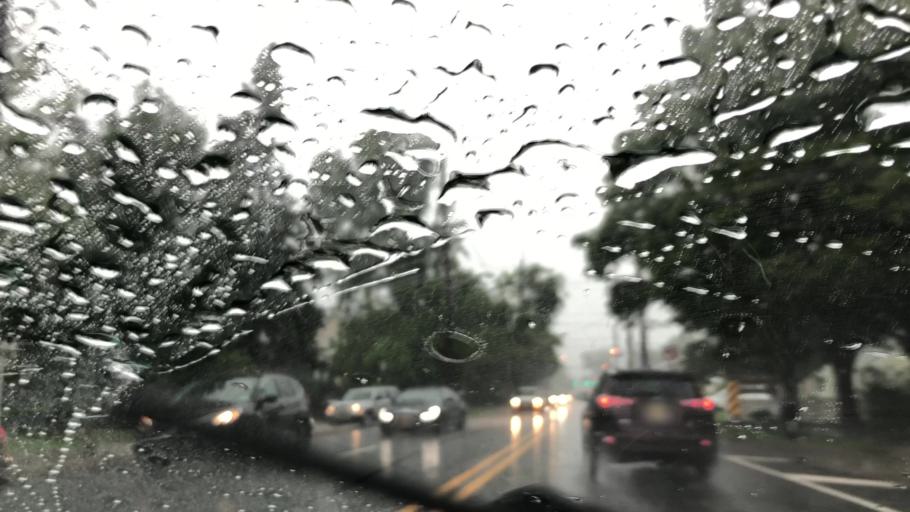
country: US
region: New Jersey
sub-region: Bergen County
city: Rochelle Park
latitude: 40.9110
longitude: -74.0726
